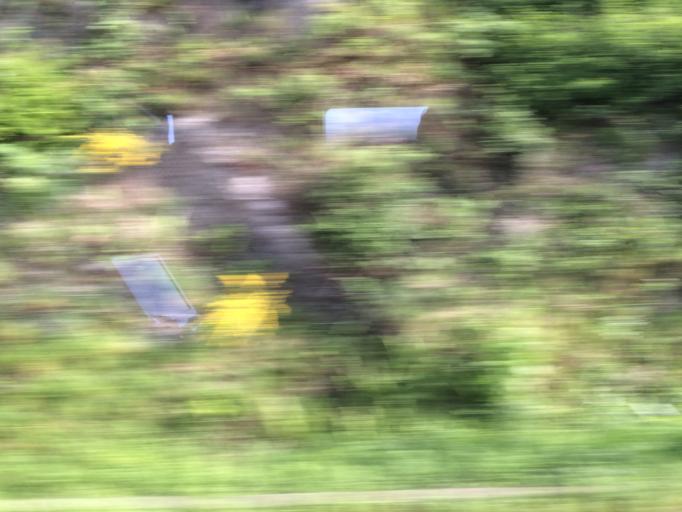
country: DE
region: Rheinland-Pfalz
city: Osterspai
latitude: 50.2430
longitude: 7.6329
